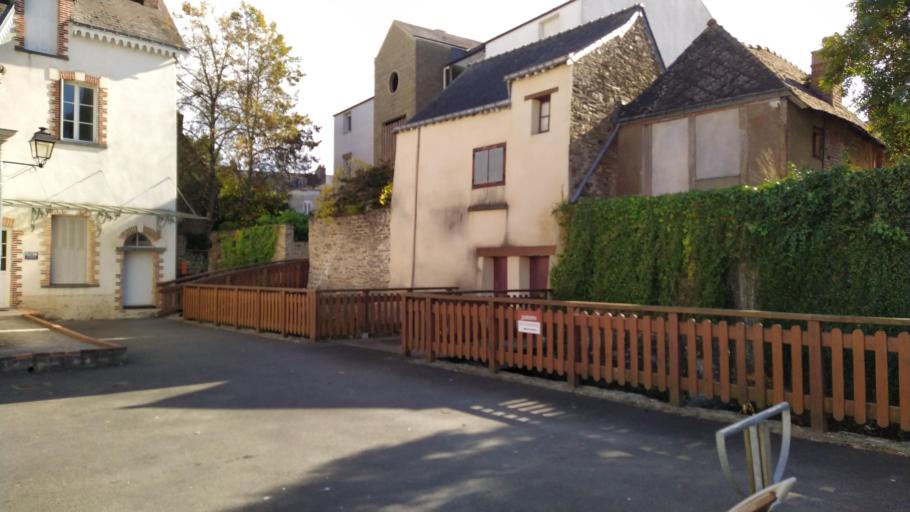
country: FR
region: Pays de la Loire
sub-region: Departement de la Loire-Atlantique
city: Chateaubriant
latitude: 47.7202
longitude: -1.3777
